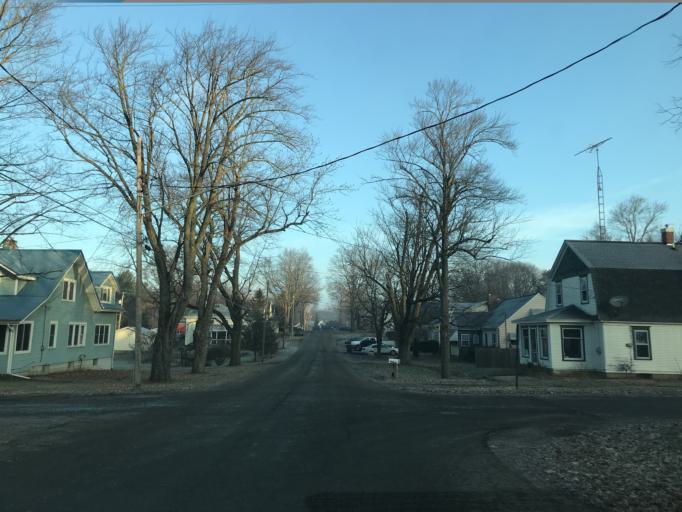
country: US
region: Michigan
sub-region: Ingham County
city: Leslie
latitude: 42.3829
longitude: -84.4611
